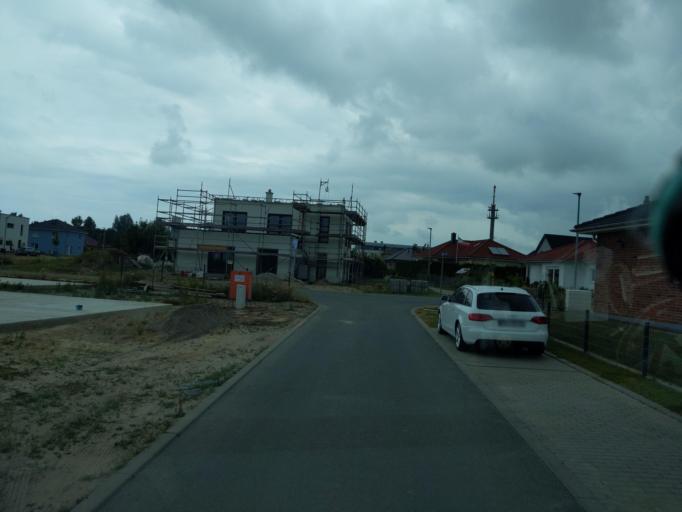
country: DE
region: Mecklenburg-Vorpommern
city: Ribnitz-Damgarten
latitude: 54.2338
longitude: 12.4424
